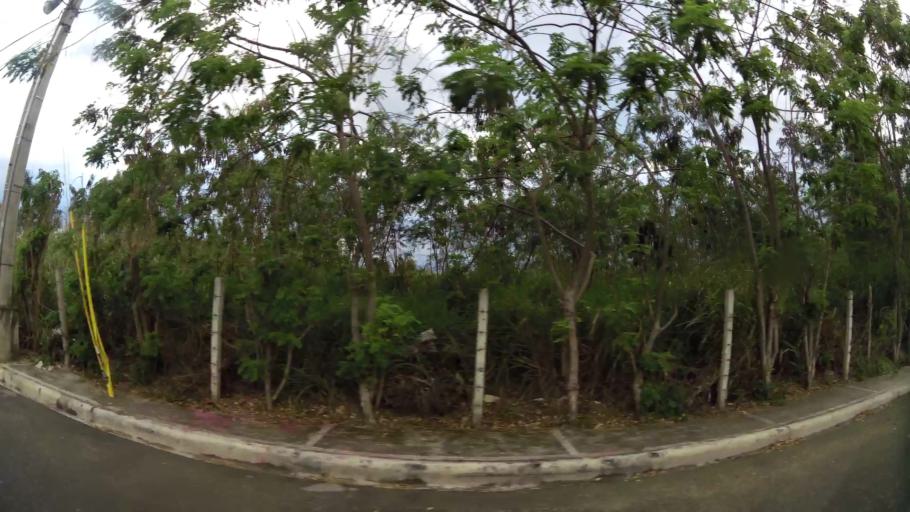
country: DO
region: Nacional
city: Santo Domingo
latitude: 18.5042
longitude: -69.9720
